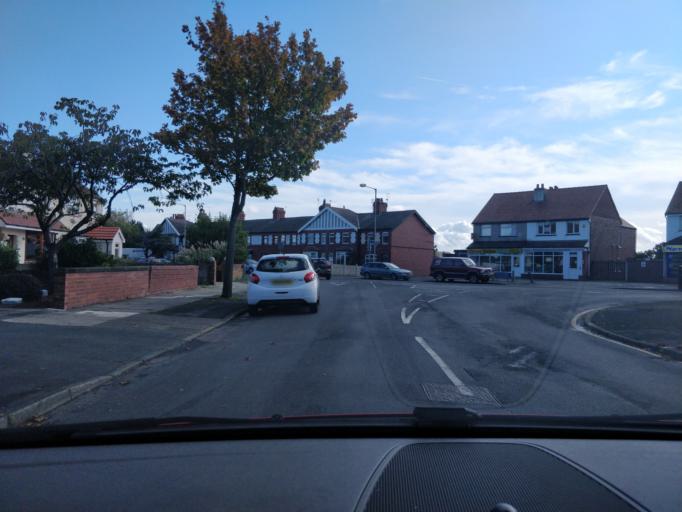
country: GB
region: England
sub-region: Sefton
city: Southport
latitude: 53.6393
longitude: -2.9778
